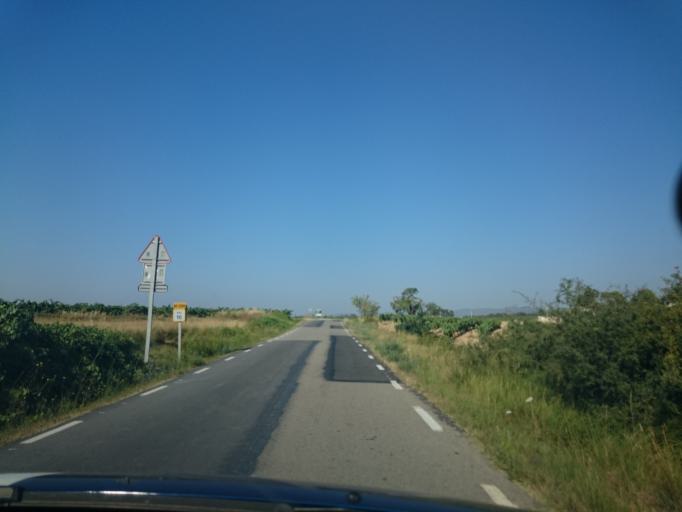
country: ES
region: Catalonia
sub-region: Provincia de Barcelona
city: el Pla del Penedes
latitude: 41.4166
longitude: 1.6832
